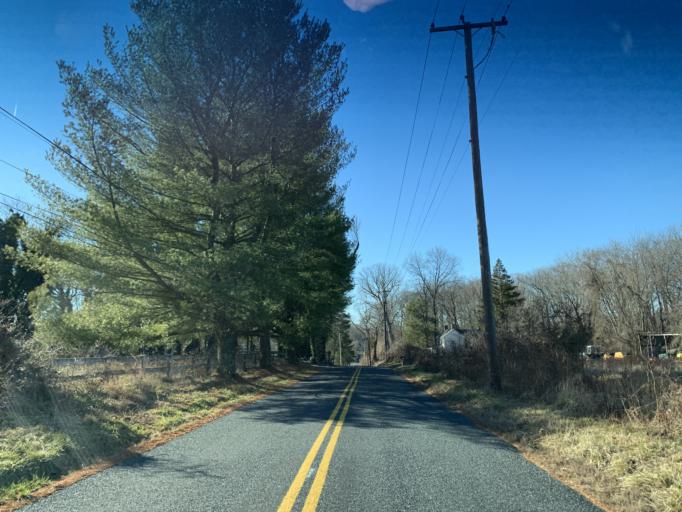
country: US
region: Maryland
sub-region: Harford County
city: Riverside
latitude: 39.5351
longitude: -76.2511
